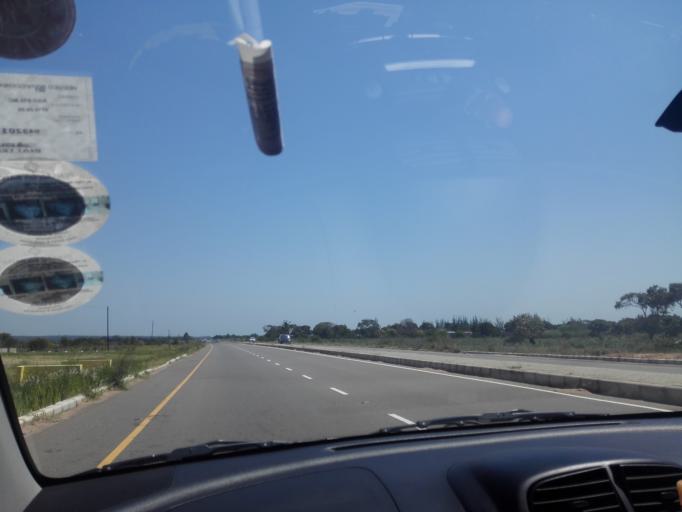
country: MZ
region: Maputo City
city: Maputo
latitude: -25.8038
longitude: 32.6729
